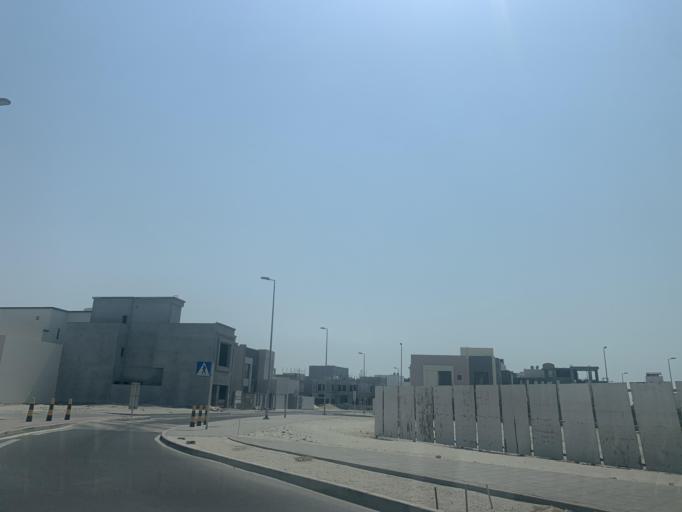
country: BH
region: Muharraq
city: Al Hadd
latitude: 26.2369
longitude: 50.6617
